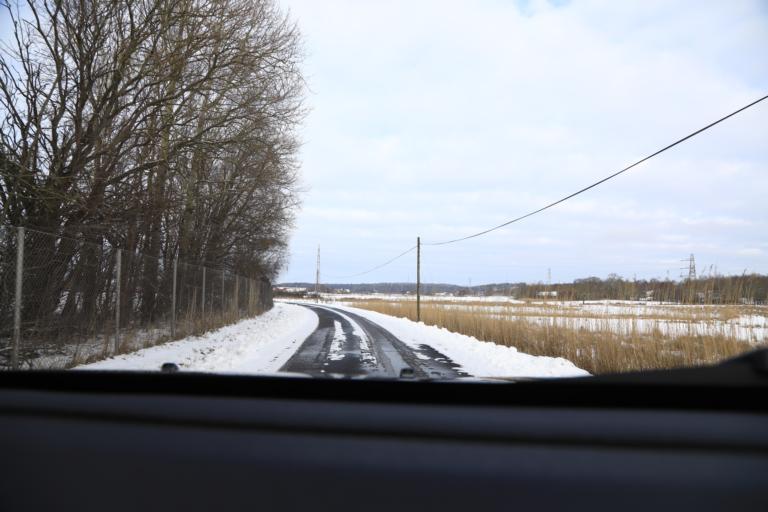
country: SE
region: Halland
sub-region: Kungsbacka Kommun
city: Frillesas
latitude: 57.2242
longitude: 12.1876
